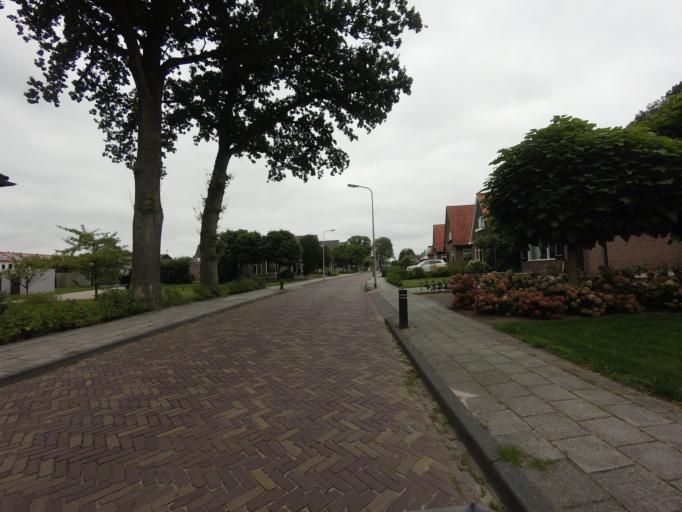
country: NL
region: Overijssel
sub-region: Gemeente Steenwijkerland
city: Steenwijkerwold
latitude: 52.8036
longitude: 6.0617
